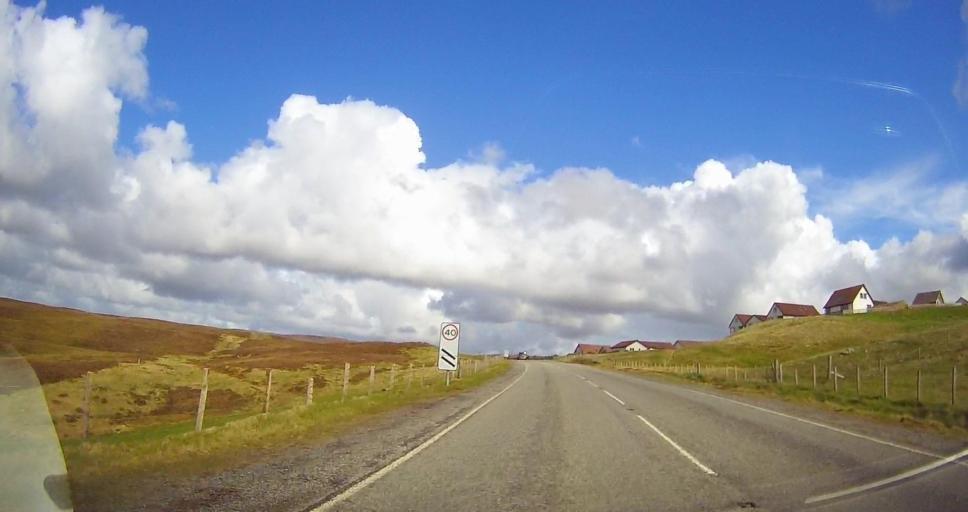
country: GB
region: Scotland
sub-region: Shetland Islands
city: Lerwick
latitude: 60.3921
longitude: -1.3756
